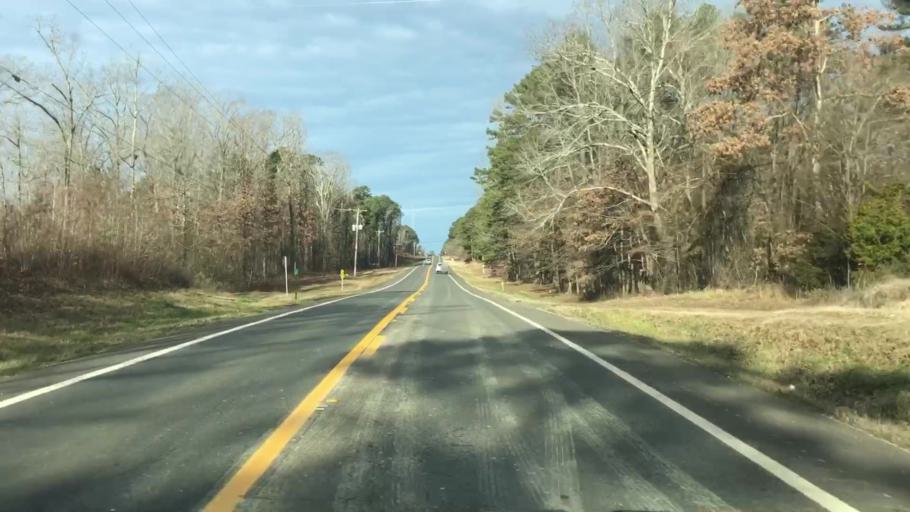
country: US
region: Arkansas
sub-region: Montgomery County
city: Mount Ida
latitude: 34.5405
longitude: -93.6064
